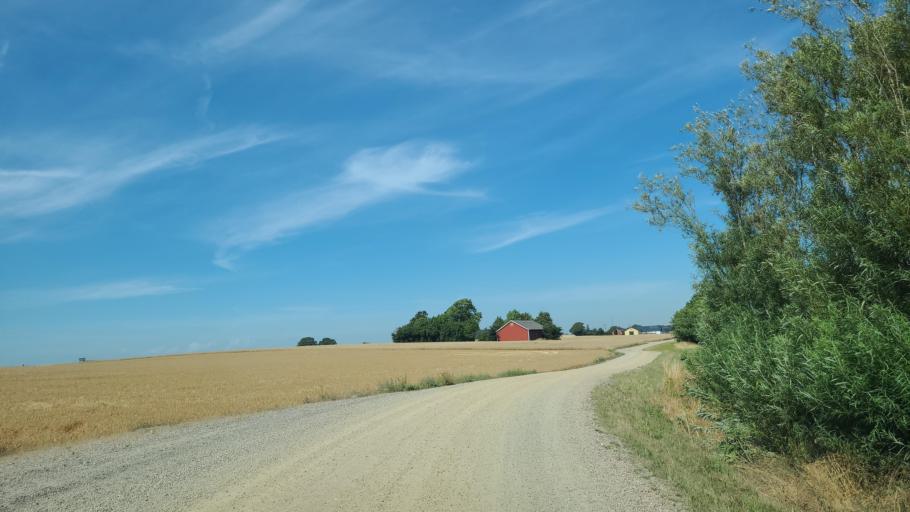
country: SE
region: Skane
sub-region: Trelleborgs Kommun
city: Skare
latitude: 55.4109
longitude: 13.0683
